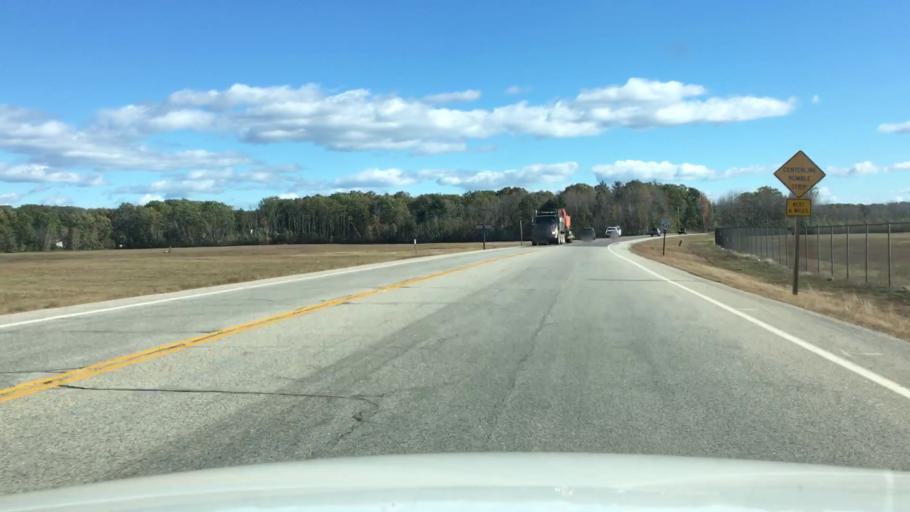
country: US
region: Maine
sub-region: York County
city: South Sanford
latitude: 43.3973
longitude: -70.6971
